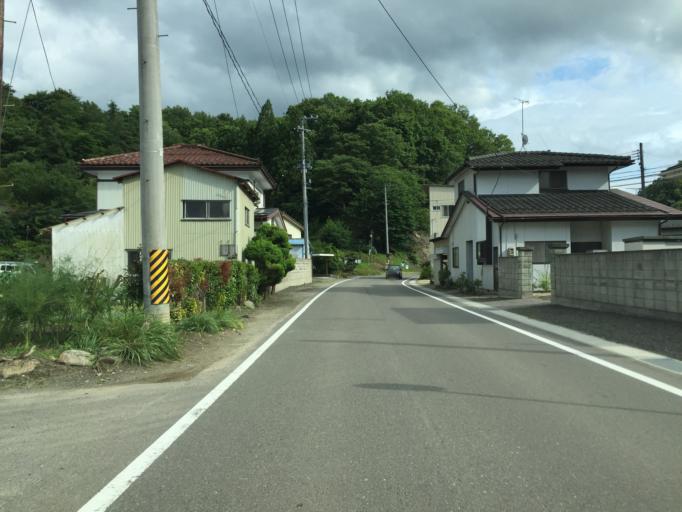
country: JP
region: Fukushima
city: Fukushima-shi
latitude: 37.6708
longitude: 140.5869
